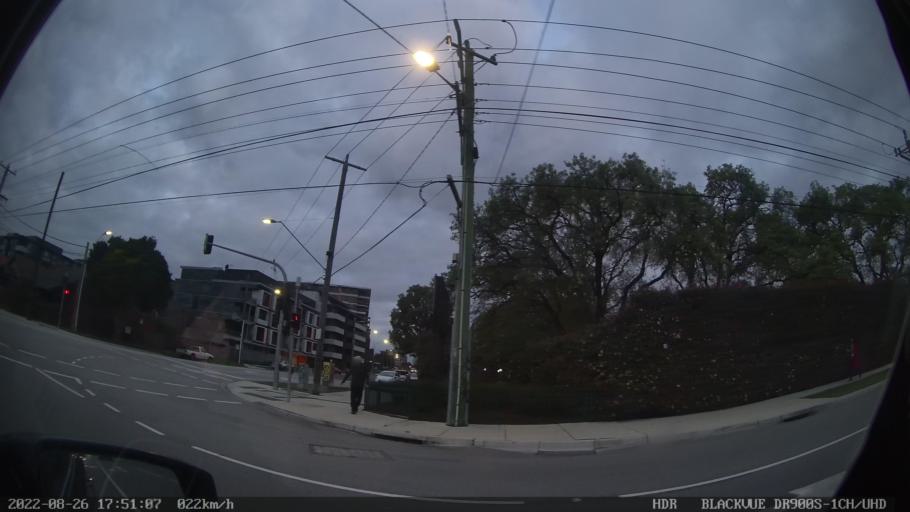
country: AU
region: Victoria
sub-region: Stonnington
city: Malvern East
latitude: -37.8769
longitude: 145.0353
